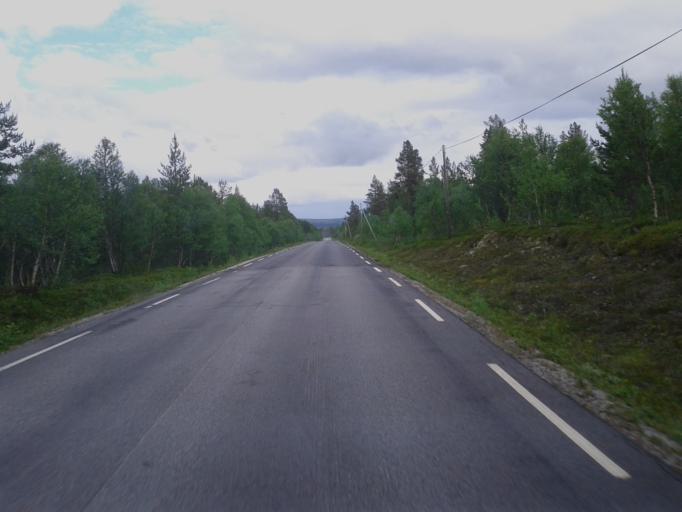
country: NO
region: Sor-Trondelag
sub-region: Roros
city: Roros
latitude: 62.3121
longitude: 11.6675
